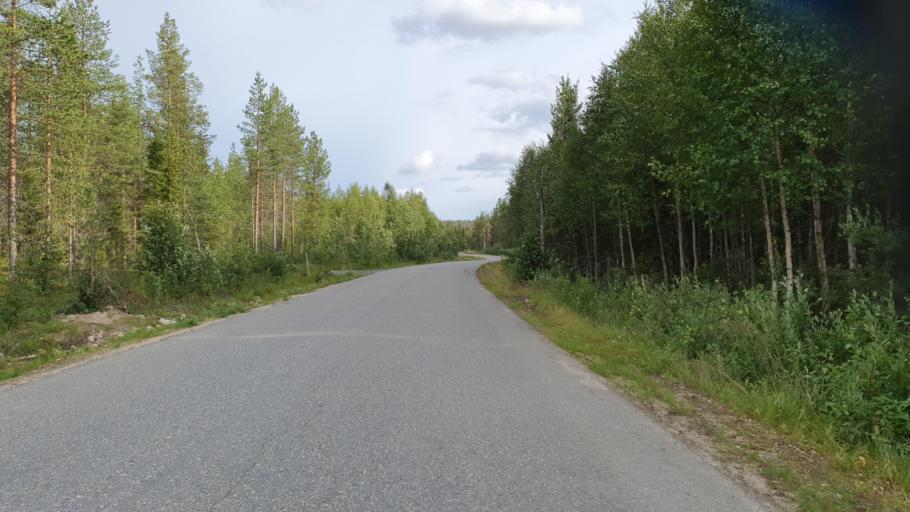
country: FI
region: Lapland
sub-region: Tunturi-Lappi
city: Kolari
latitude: 67.6000
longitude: 24.1639
